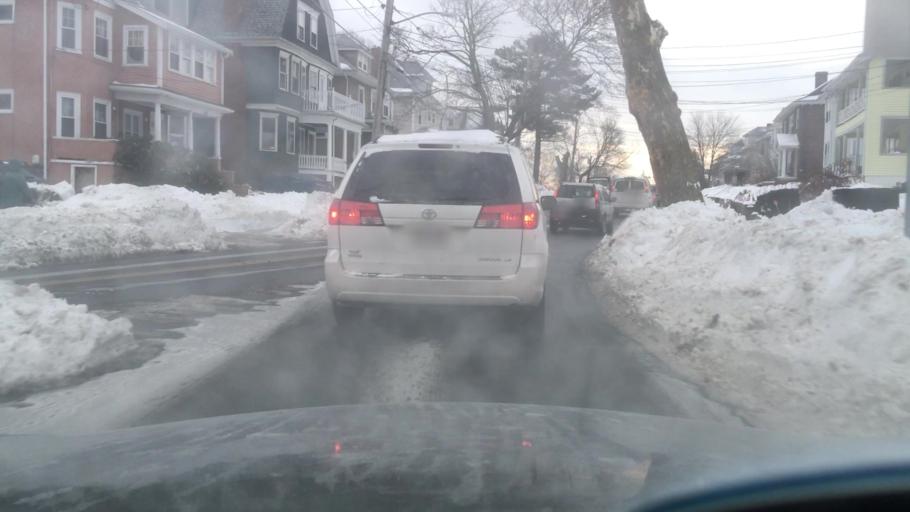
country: US
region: Massachusetts
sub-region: Middlesex County
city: Watertown
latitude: 42.3765
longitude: -71.1643
